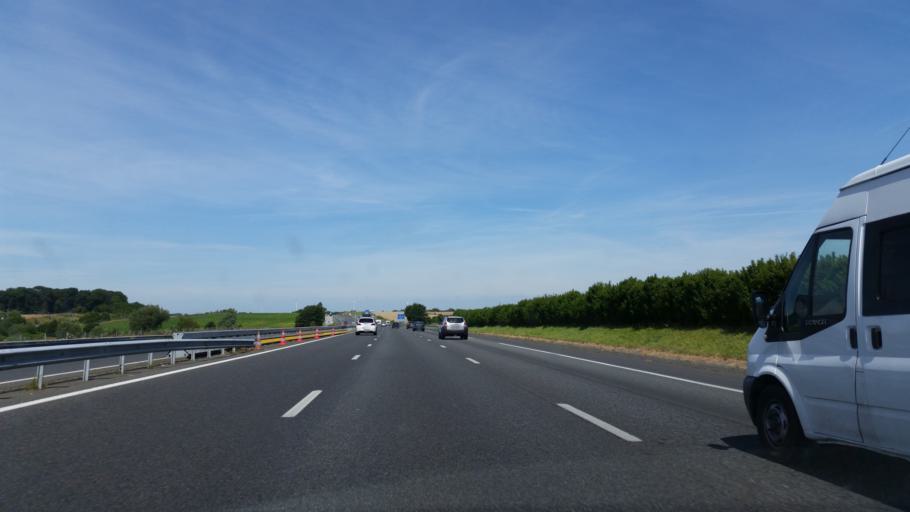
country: FR
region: Nord-Pas-de-Calais
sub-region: Departement du Pas-de-Calais
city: Croisilles
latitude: 50.1773
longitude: 2.8746
